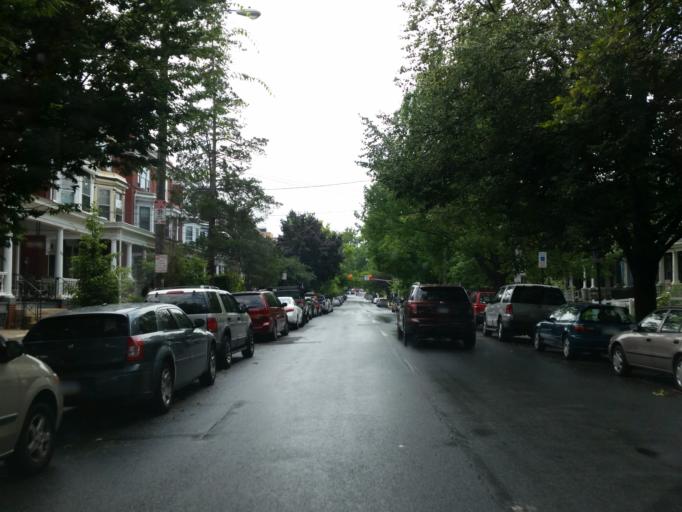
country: US
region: Pennsylvania
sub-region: Lancaster County
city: Lancaster
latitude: 40.0511
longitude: -76.3061
